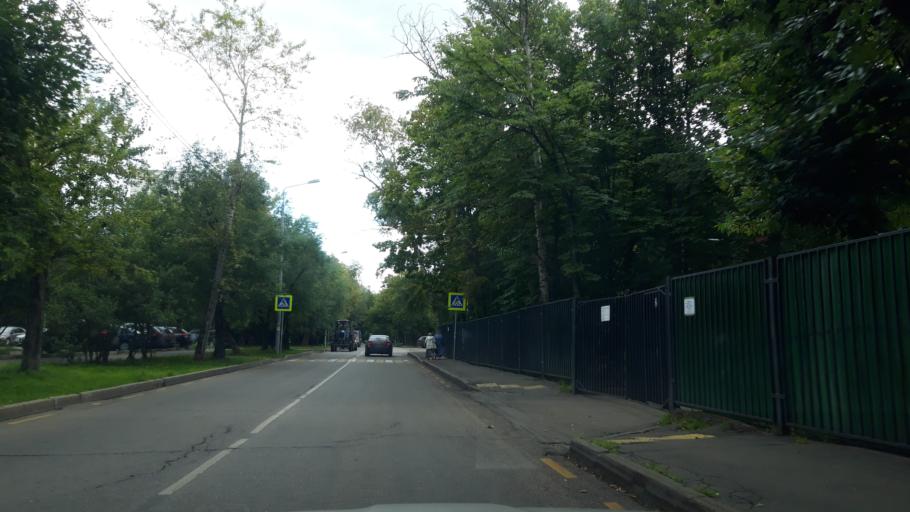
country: RU
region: Moskovskaya
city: Levoberezhnyy
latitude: 55.8479
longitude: 37.4806
